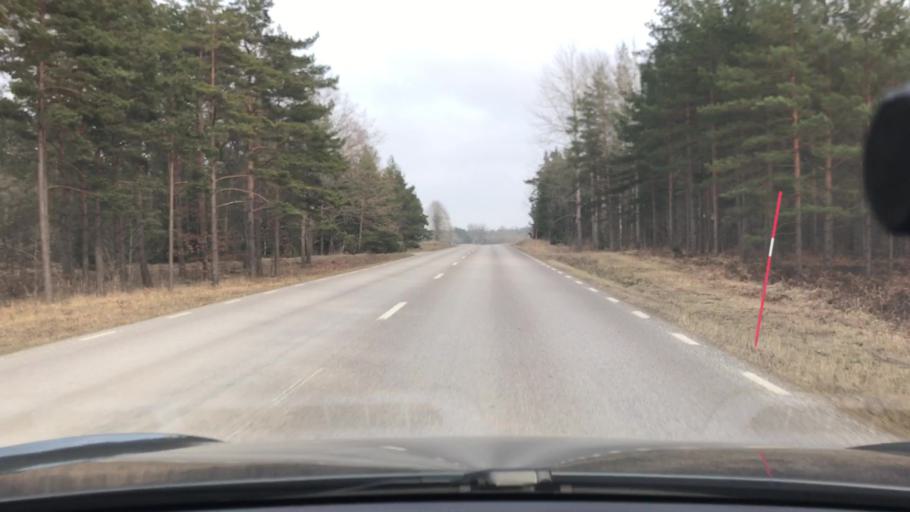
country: SE
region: Gotland
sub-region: Gotland
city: Slite
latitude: 57.4353
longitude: 18.6745
